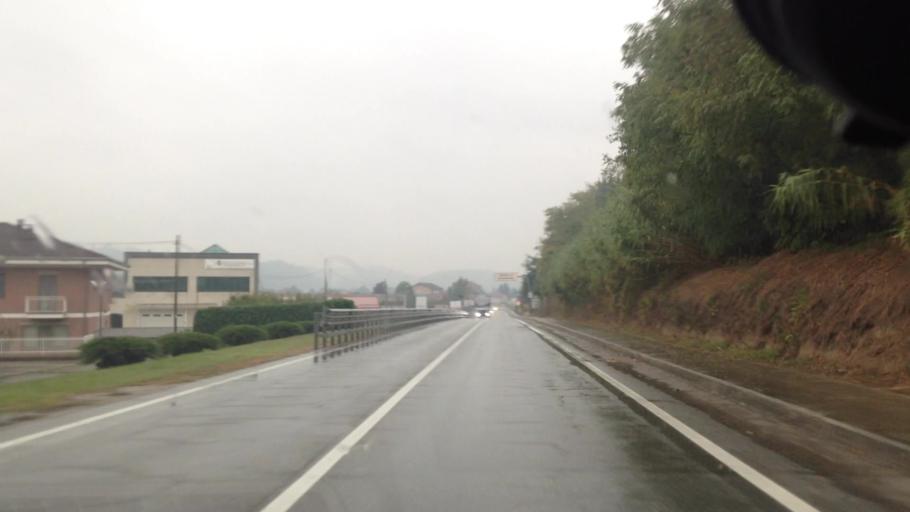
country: IT
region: Piedmont
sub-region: Provincia di Asti
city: Castello di Annone
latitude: 44.8783
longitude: 8.3268
